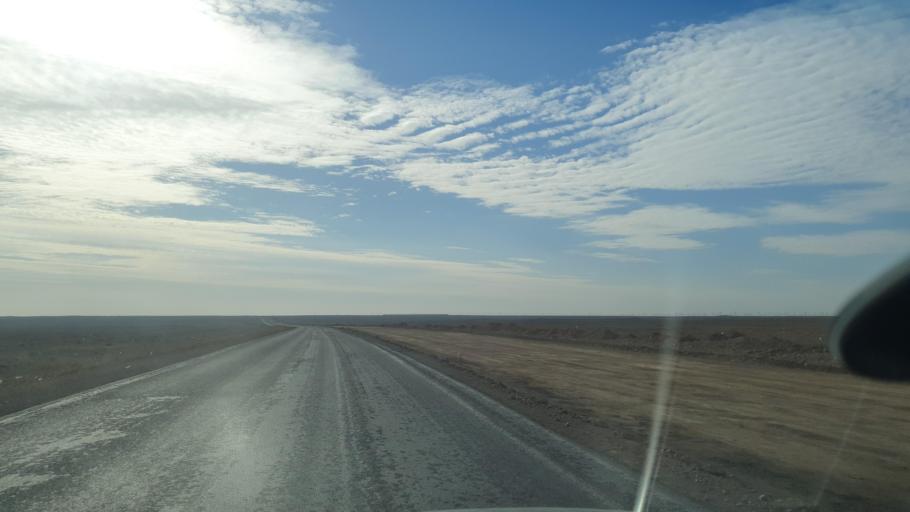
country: KZ
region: Qaraghandy
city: Saryshaghan
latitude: 45.9690
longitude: 73.5479
